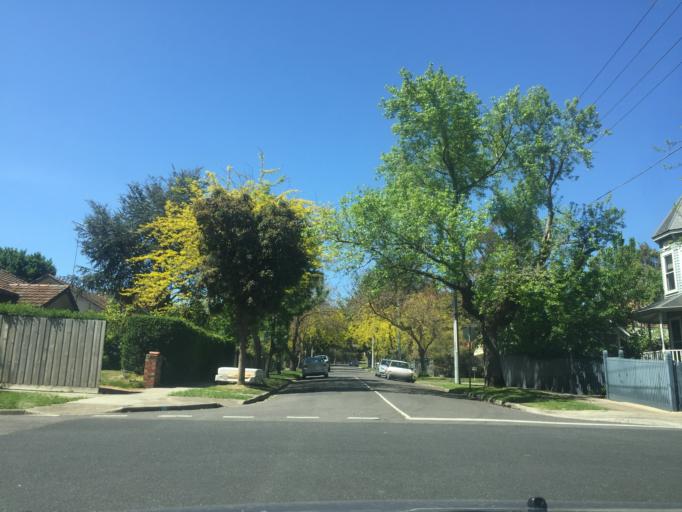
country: AU
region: Victoria
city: Ivanhoe East
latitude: -37.7680
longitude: 145.0563
